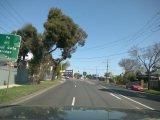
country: AU
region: Victoria
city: Spotswood
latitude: -37.8205
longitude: 144.8837
